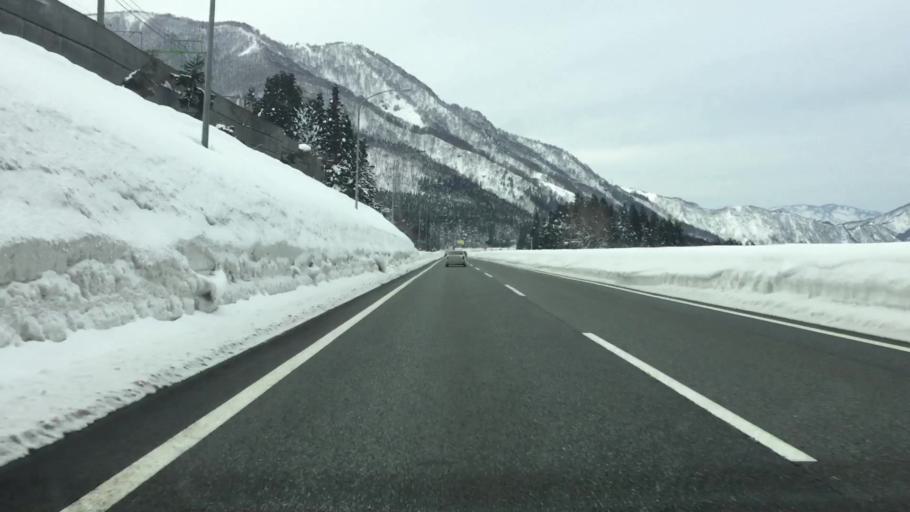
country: JP
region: Niigata
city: Shiozawa
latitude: 36.8773
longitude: 138.8595
